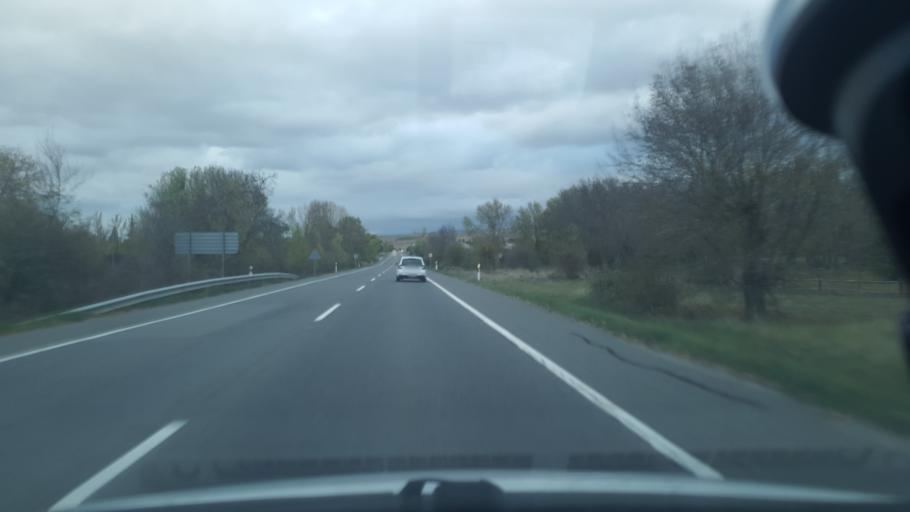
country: ES
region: Castille and Leon
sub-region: Provincia de Segovia
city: Ortigosa del Monte
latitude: 40.8941
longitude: -4.1863
